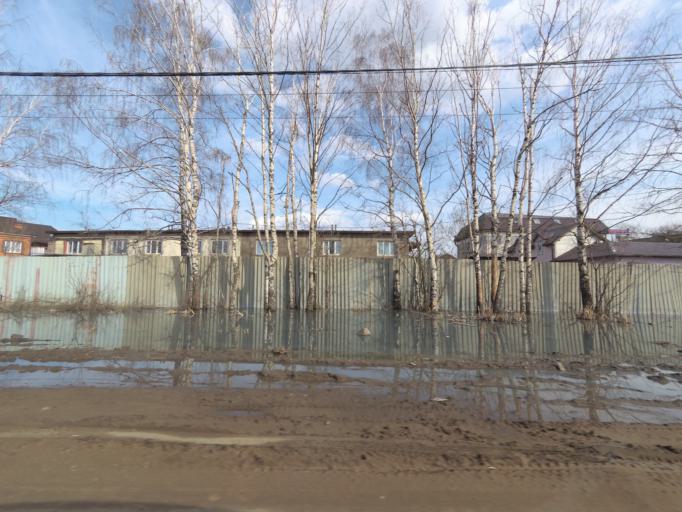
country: RU
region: Moskovskaya
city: Lobnya
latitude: 55.9914
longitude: 37.4167
